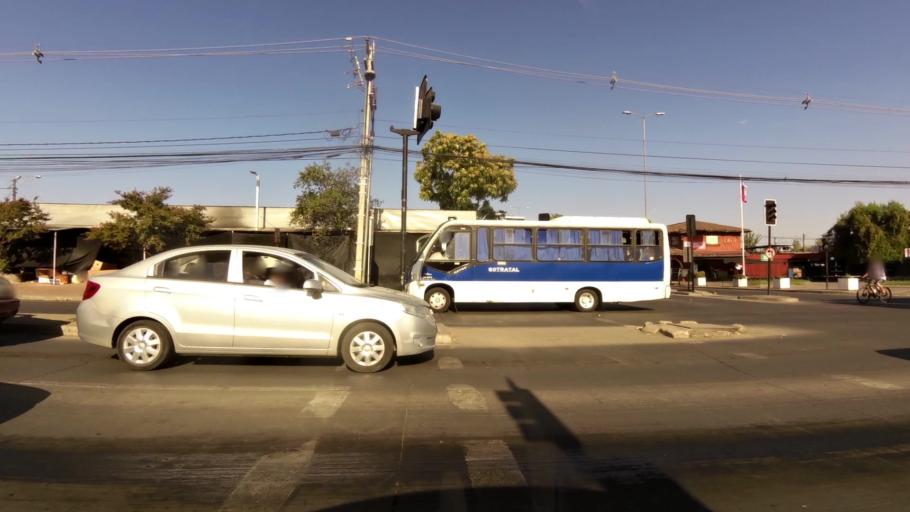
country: CL
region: Maule
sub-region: Provincia de Talca
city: Talca
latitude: -35.4230
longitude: -71.6498
